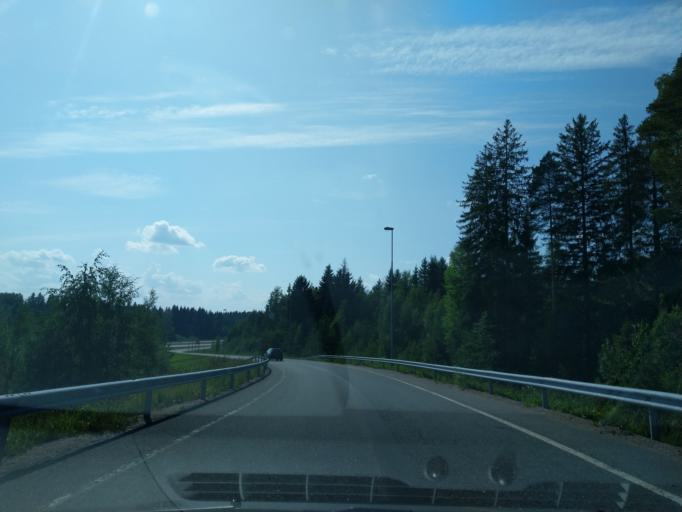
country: FI
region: South Karelia
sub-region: Lappeenranta
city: Lappeenranta
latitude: 61.0362
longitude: 28.1144
